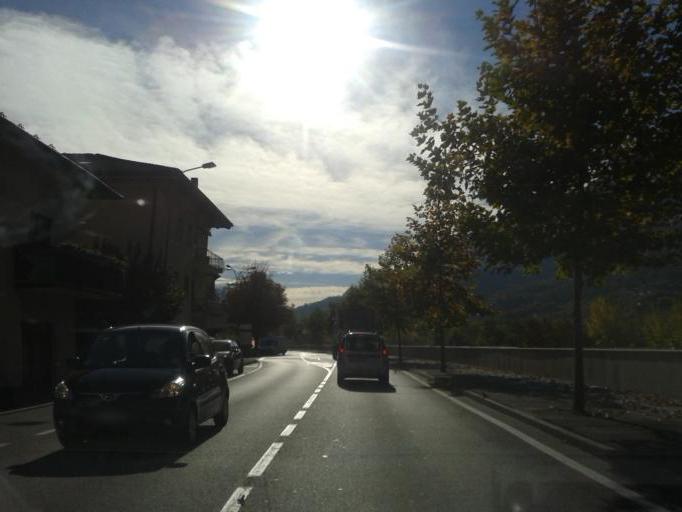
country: IT
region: Trentino-Alto Adige
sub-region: Provincia di Trento
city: Ravina
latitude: 46.0521
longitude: 11.1119
